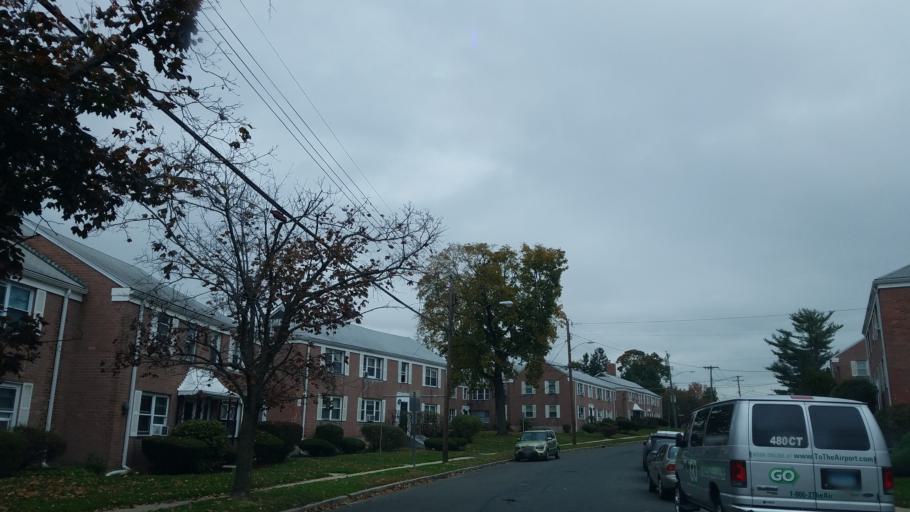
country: US
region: Connecticut
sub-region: Fairfield County
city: Stamford
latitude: 41.0578
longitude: -73.5183
